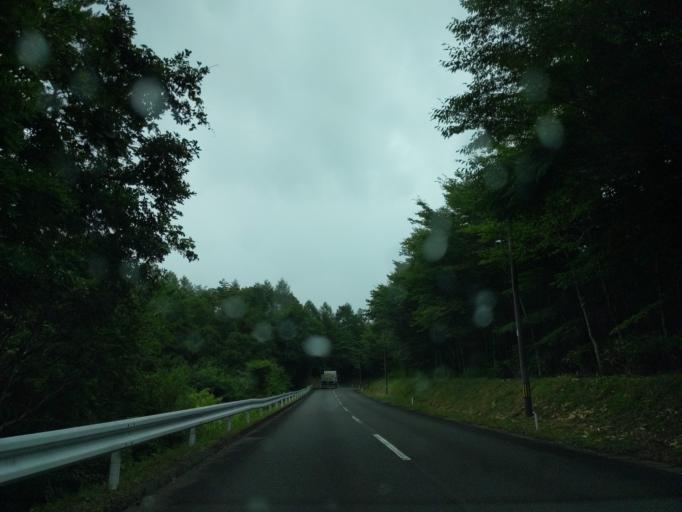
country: JP
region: Fukushima
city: Sukagawa
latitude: 37.2621
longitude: 140.0950
